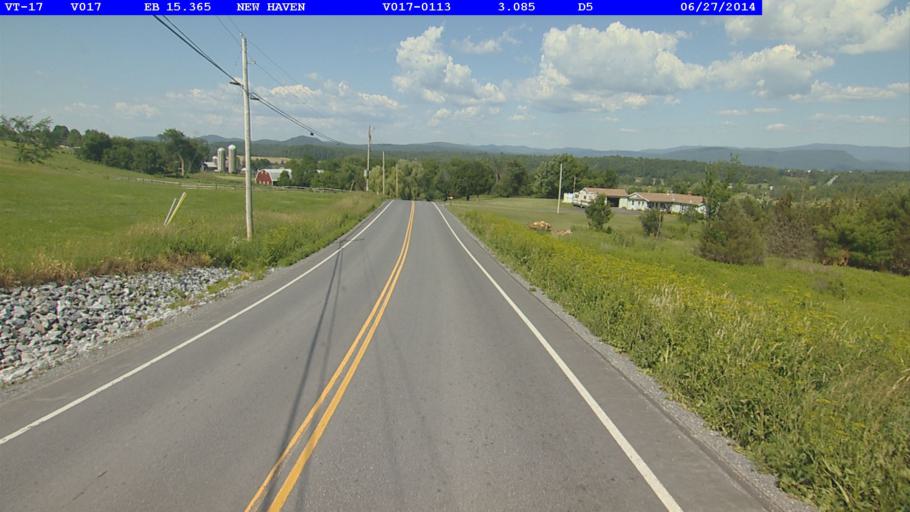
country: US
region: Vermont
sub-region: Addison County
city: Vergennes
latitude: 44.1201
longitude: -73.1892
